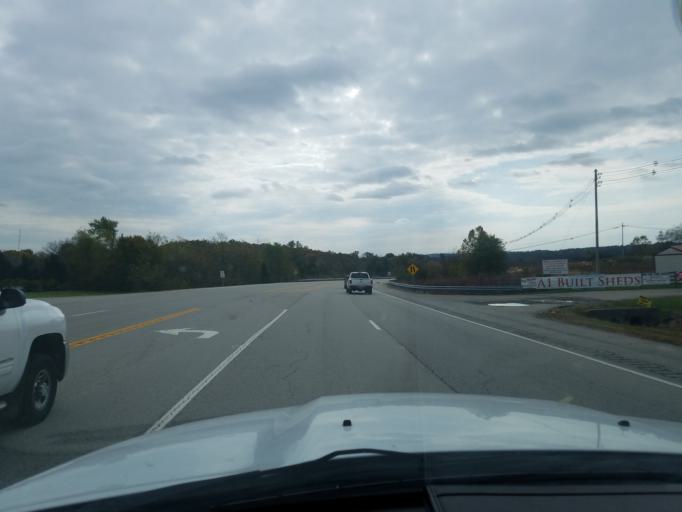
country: US
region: Kentucky
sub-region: Bullitt County
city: Mount Washington
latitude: 38.0511
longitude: -85.5361
